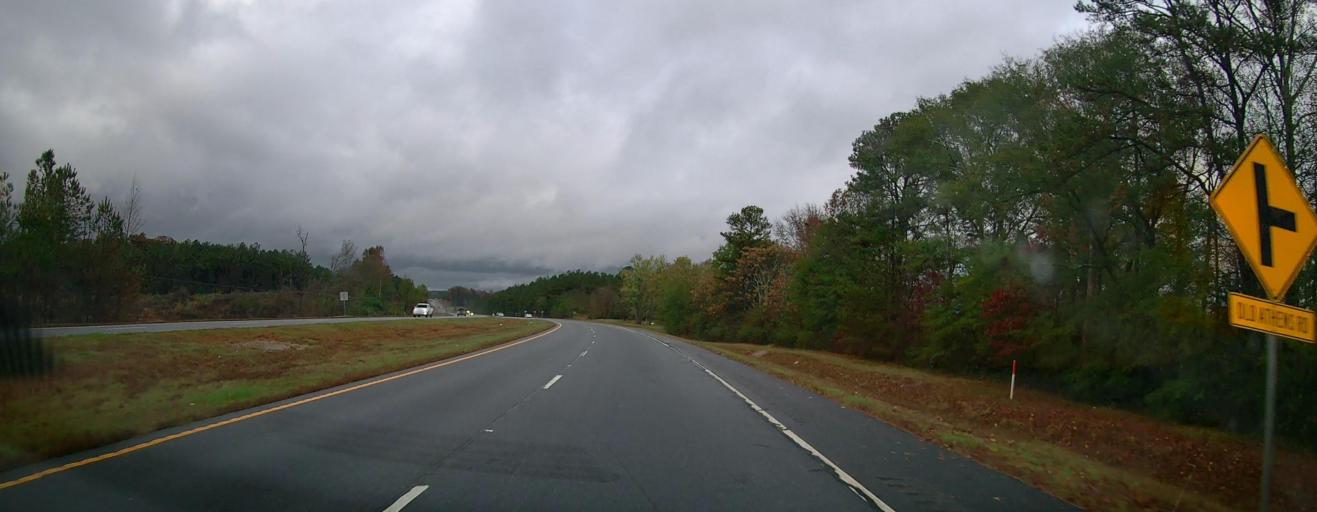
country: US
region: Georgia
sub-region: Jackson County
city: Nicholson
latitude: 34.0835
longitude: -83.4236
